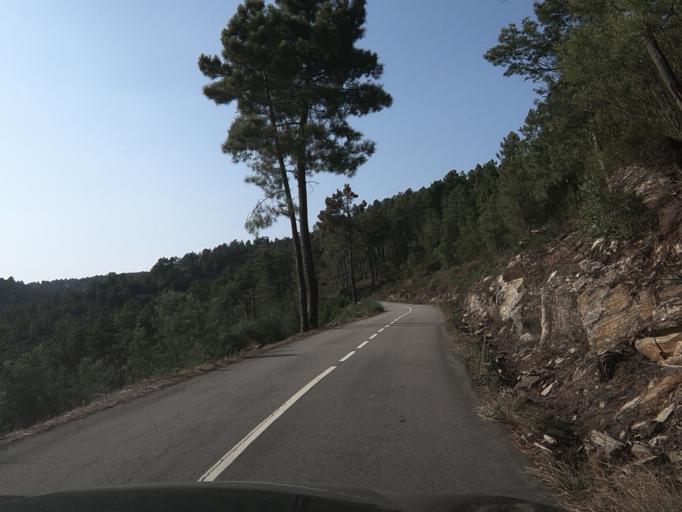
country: PT
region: Vila Real
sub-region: Sabrosa
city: Vilela
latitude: 41.2140
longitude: -7.6180
